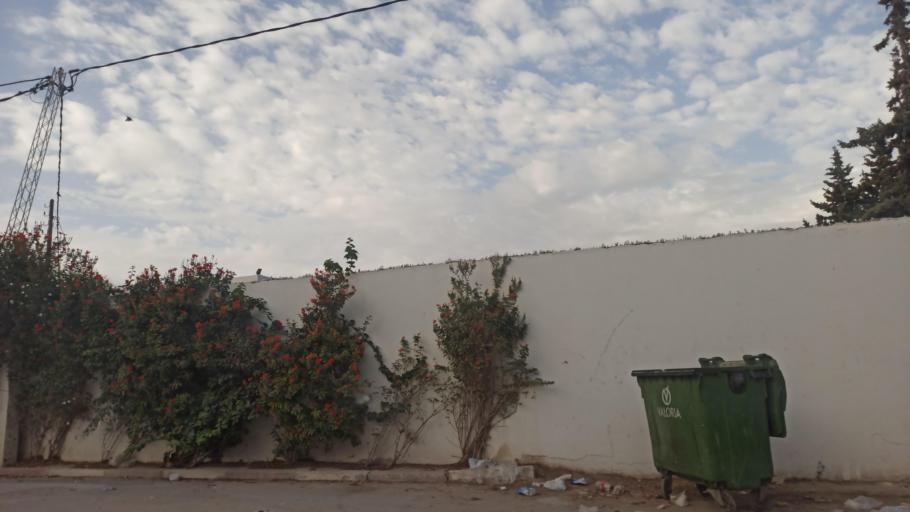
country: TN
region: Tunis
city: Al Marsa
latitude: 36.8714
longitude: 10.2655
